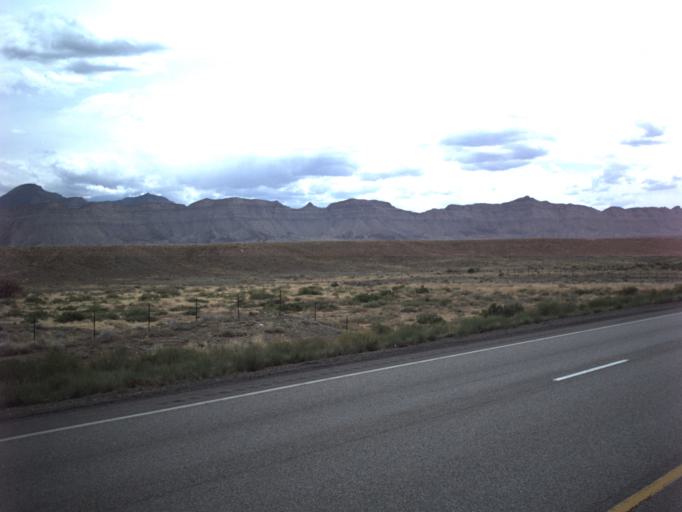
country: US
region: Utah
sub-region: Carbon County
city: East Carbon City
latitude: 39.3806
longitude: -110.4060
